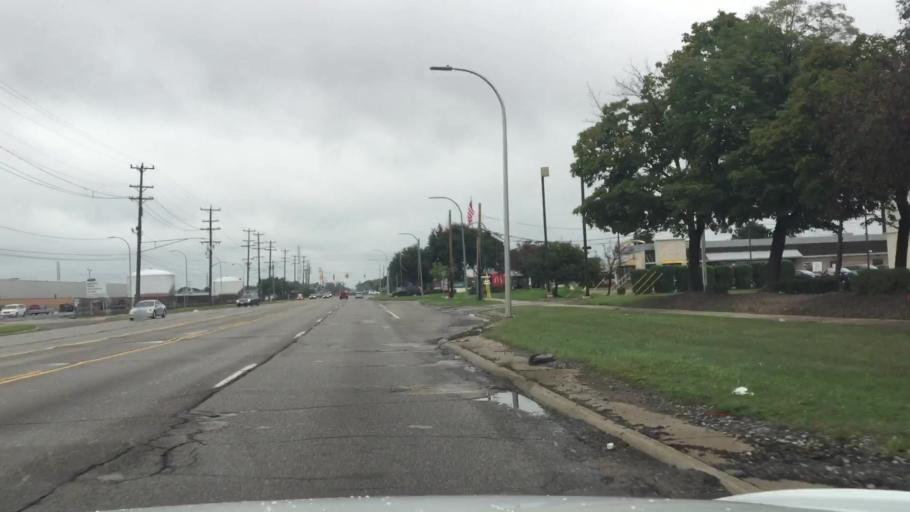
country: US
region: Michigan
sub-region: Wayne County
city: Livonia
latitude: 42.3709
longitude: -83.3331
